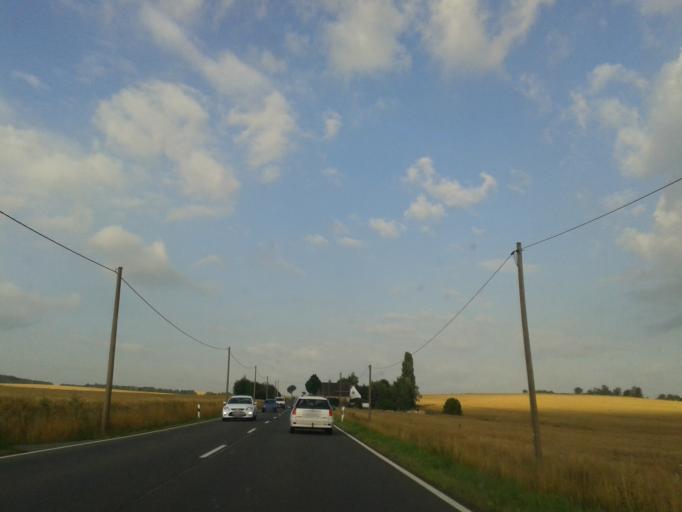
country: DE
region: Saxony
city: Wilsdruff
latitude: 51.0272
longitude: 13.5364
